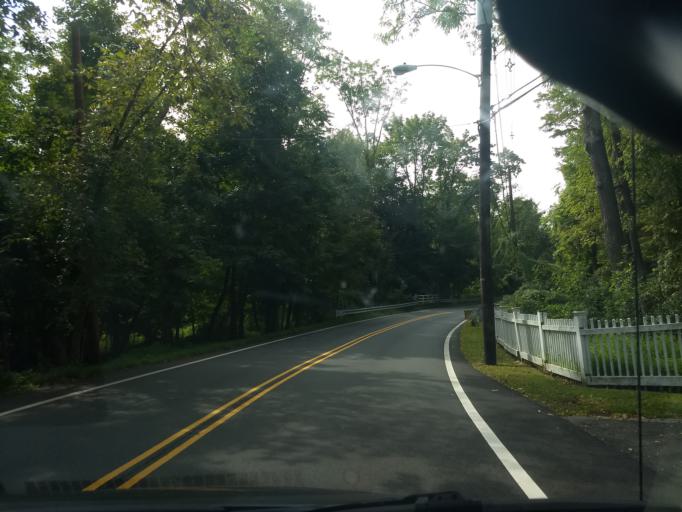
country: US
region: New Jersey
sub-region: Morris County
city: Morris Plains
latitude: 40.8236
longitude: -74.4935
